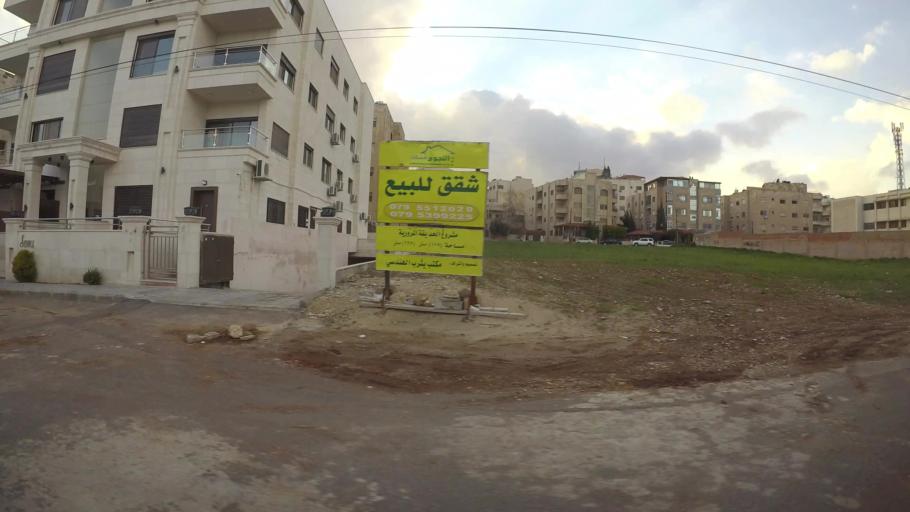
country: JO
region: Amman
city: Al Jubayhah
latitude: 31.9847
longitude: 35.8623
